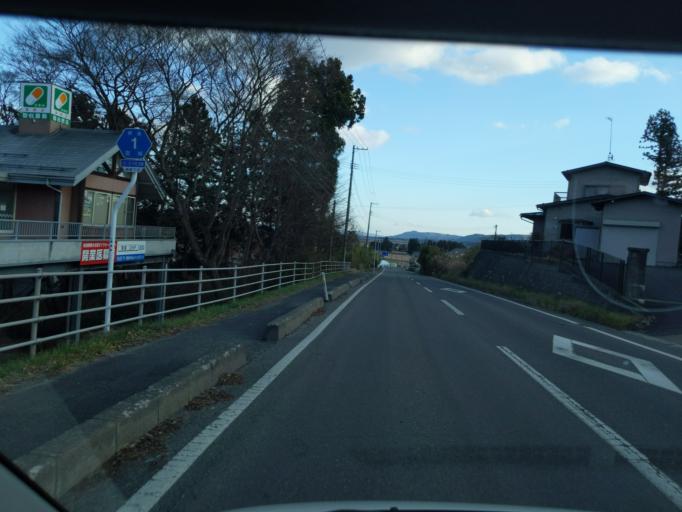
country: JP
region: Miyagi
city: Kogota
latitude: 38.6523
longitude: 141.0730
